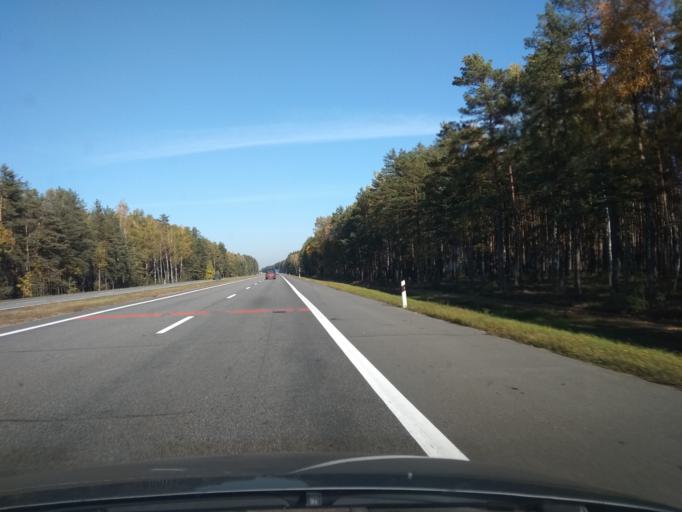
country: BY
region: Brest
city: Baranovichi
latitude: 52.9632
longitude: 25.7299
